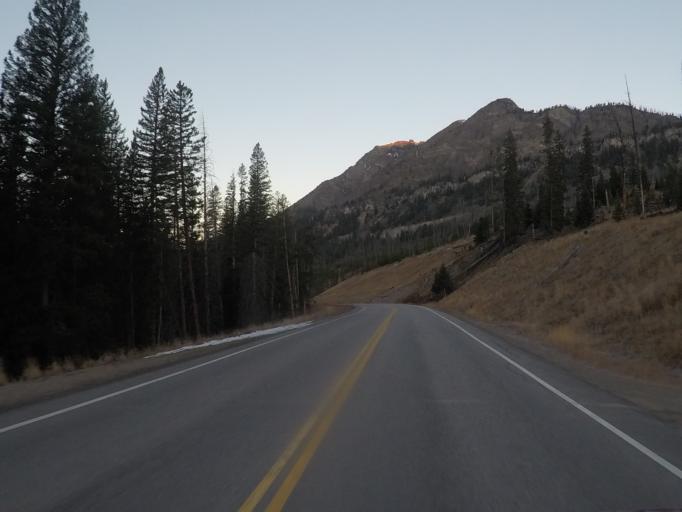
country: US
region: Montana
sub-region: Stillwater County
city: Absarokee
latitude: 45.0182
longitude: -109.9532
